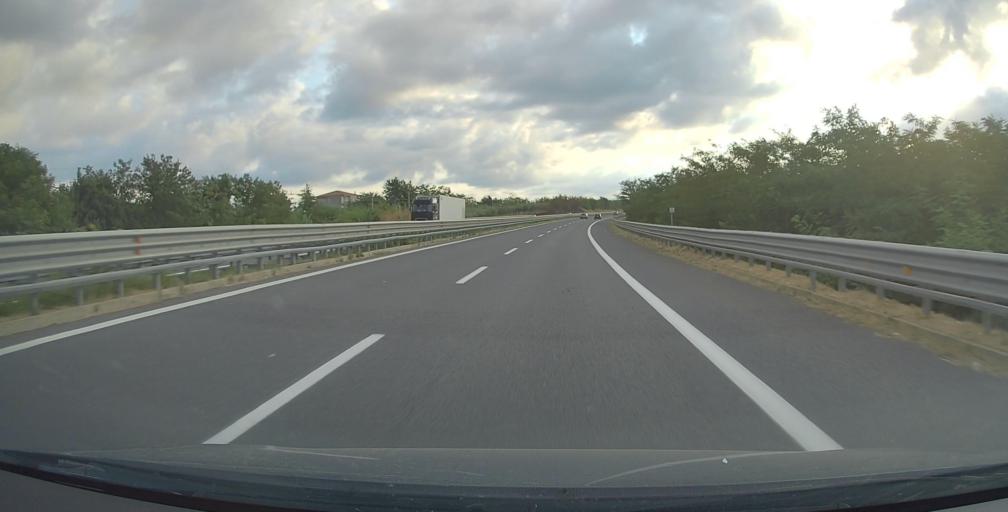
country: IT
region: Calabria
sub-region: Provincia di Catanzaro
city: Acconia
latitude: 38.8193
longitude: 16.2391
